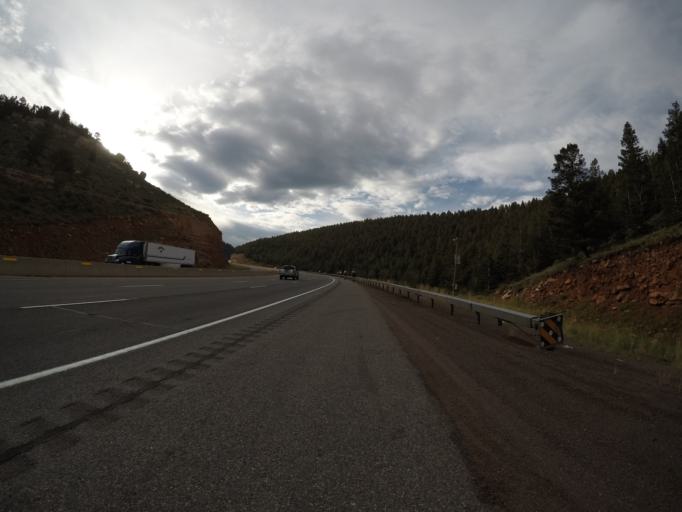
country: US
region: Wyoming
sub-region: Albany County
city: Laramie
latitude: 41.2667
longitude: -105.4761
